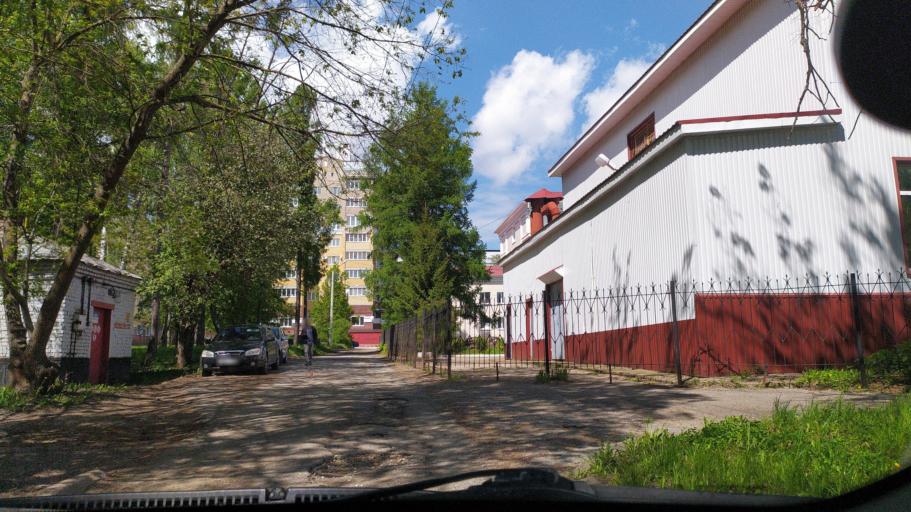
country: RU
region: Chuvashia
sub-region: Cheboksarskiy Rayon
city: Cheboksary
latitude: 56.1406
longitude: 47.2032
